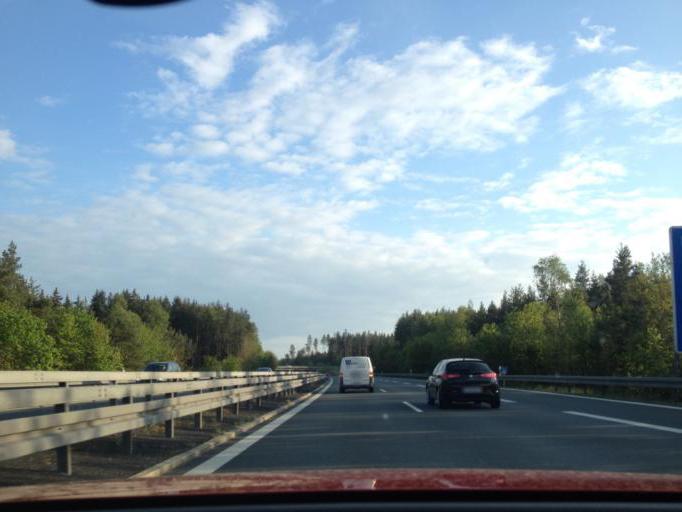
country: DE
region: Bavaria
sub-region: Upper Palatinate
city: Wiesau
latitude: 49.8631
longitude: 12.1816
